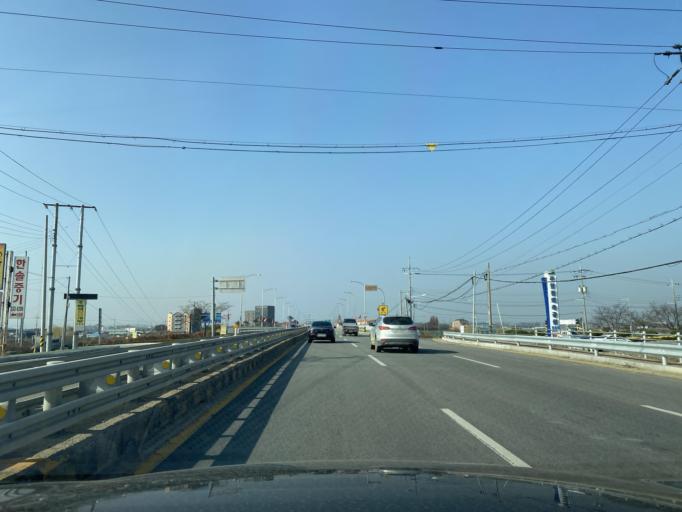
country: KR
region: Chungcheongnam-do
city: Yesan
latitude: 36.6836
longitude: 126.8237
